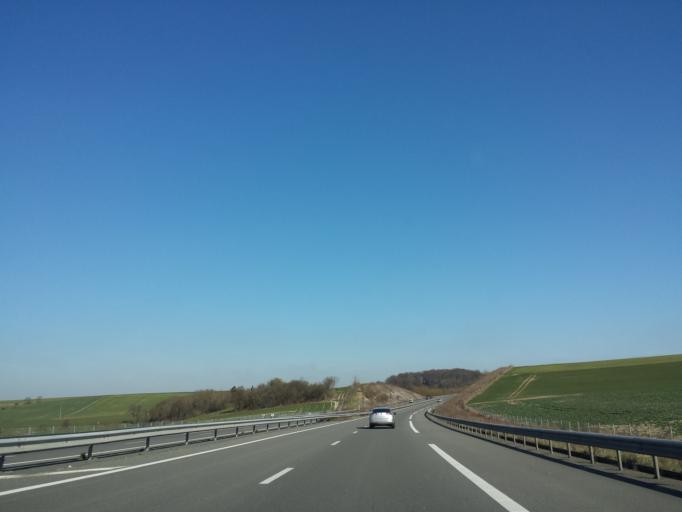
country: FR
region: Picardie
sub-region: Departement de la Somme
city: Conty
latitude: 49.6722
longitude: 2.2093
